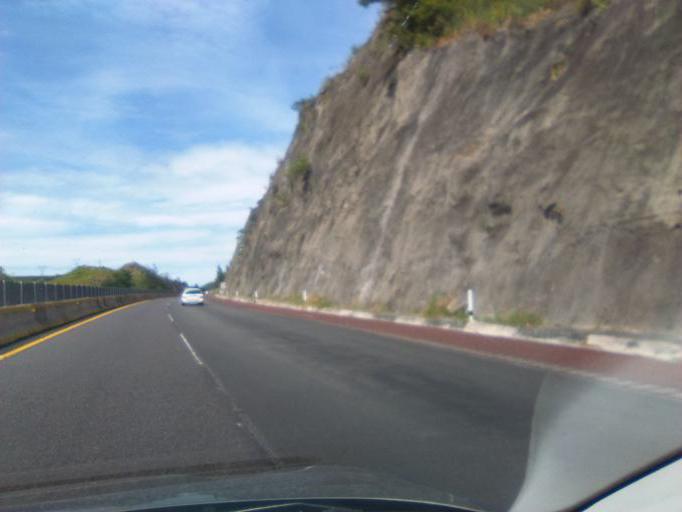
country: MX
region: Guerrero
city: Mazatlan
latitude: 17.4111
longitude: -99.4642
